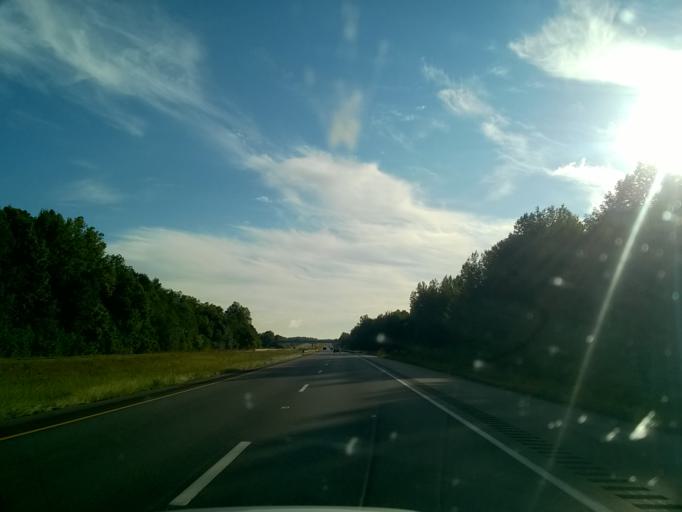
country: US
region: Indiana
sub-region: Warrick County
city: Chandler
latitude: 38.1862
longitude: -87.3583
